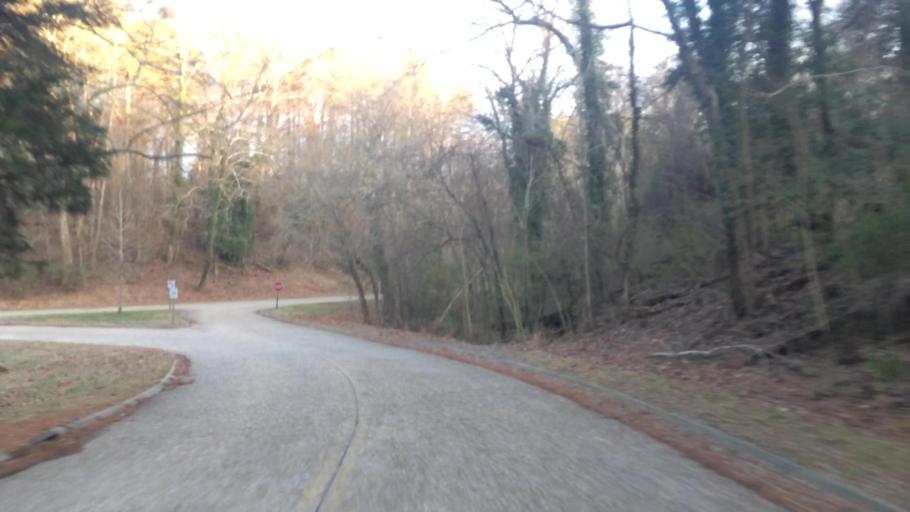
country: US
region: Virginia
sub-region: City of Williamsburg
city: Williamsburg
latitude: 37.2662
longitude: -76.7032
